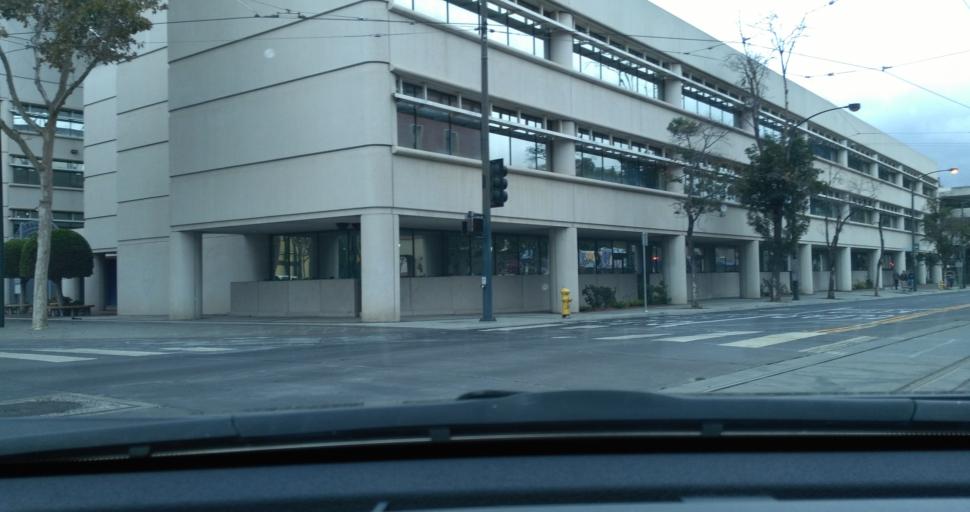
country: US
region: California
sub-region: Santa Clara County
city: San Jose
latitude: 37.3315
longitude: -121.8871
